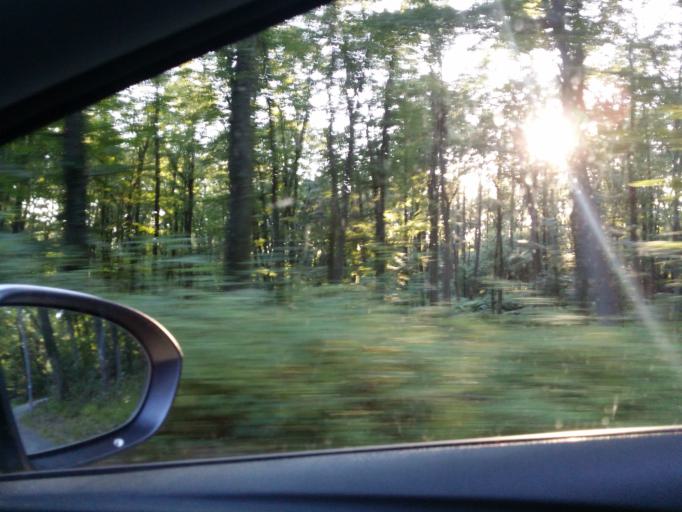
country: DE
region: Hesse
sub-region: Regierungsbezirk Darmstadt
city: Darmstadt
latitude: 49.8420
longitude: 8.6551
